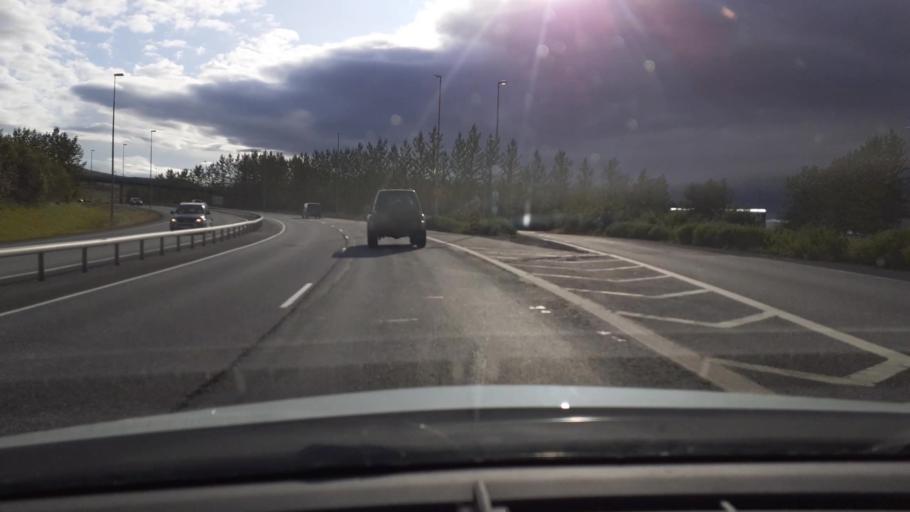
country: IS
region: Capital Region
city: Mosfellsbaer
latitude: 64.1679
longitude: -21.6878
